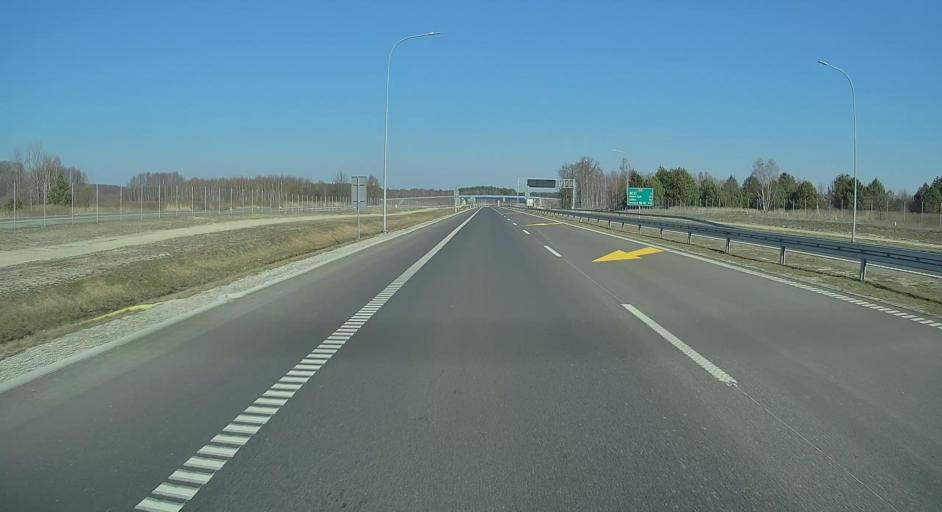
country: PL
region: Subcarpathian Voivodeship
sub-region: Powiat nizanski
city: Jarocin
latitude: 50.5799
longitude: 22.2517
